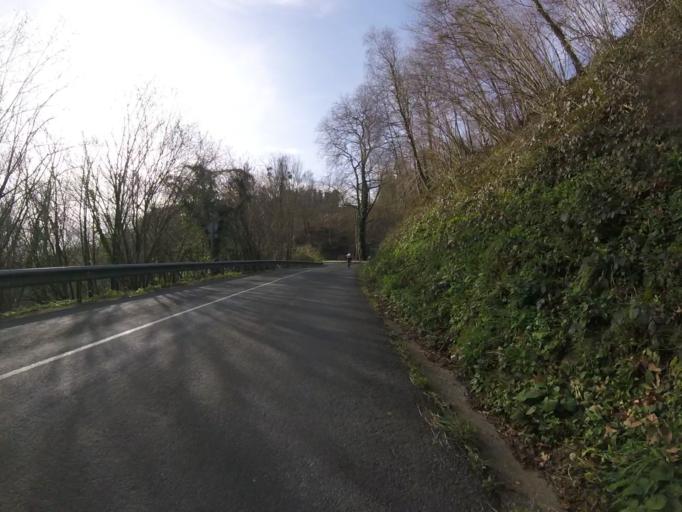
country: ES
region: Basque Country
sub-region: Provincia de Guipuzcoa
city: Asteasu
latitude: 43.2058
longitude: -2.1170
